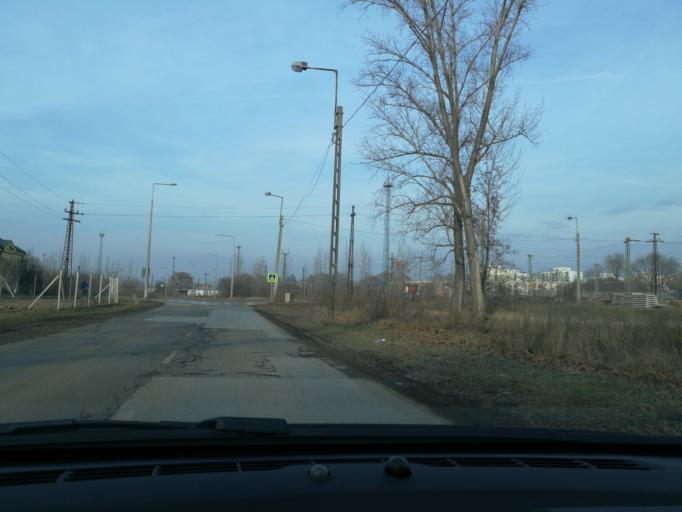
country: HU
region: Szabolcs-Szatmar-Bereg
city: Nyiregyhaza
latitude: 47.9397
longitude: 21.7076
